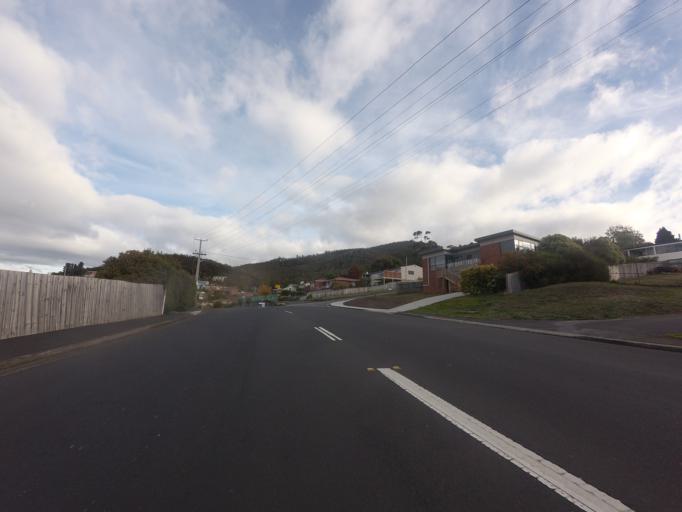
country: AU
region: Tasmania
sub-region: Glenorchy
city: Berriedale
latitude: -42.8149
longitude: 147.2404
